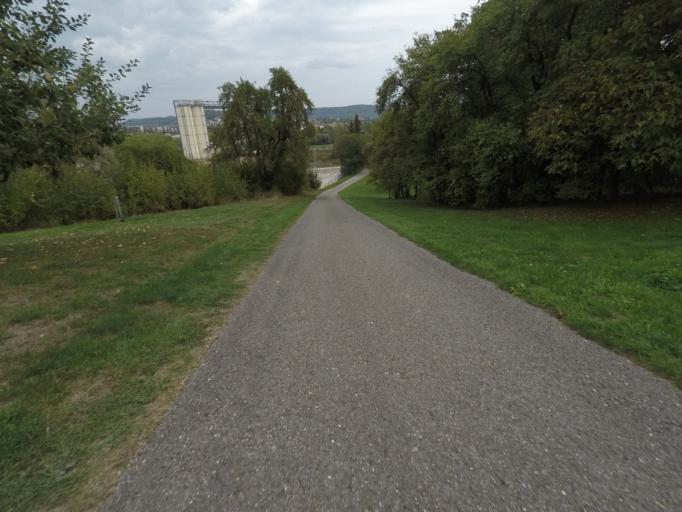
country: DE
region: Baden-Wuerttemberg
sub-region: Regierungsbezirk Stuttgart
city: Herrenberg
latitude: 48.5843
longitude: 8.8479
